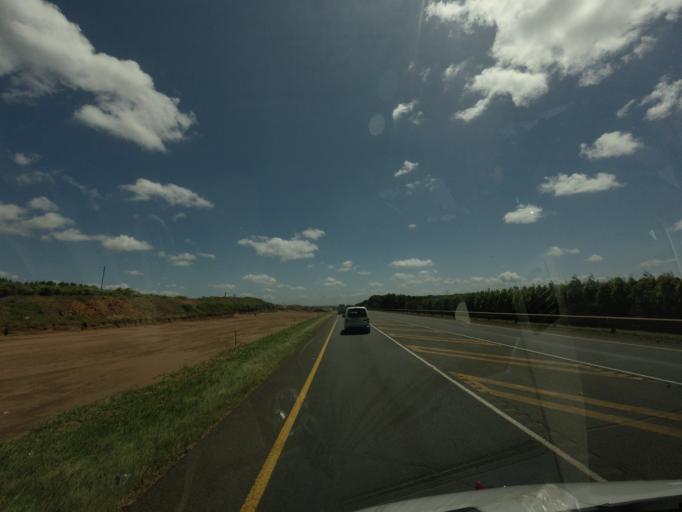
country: ZA
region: KwaZulu-Natal
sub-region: uThungulu District Municipality
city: Empangeni
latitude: -28.7998
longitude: 31.9201
